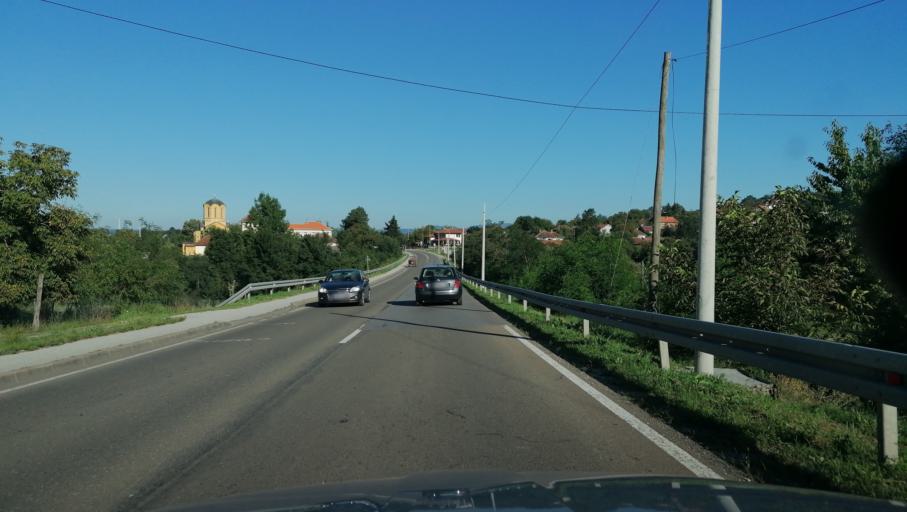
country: RS
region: Central Serbia
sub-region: Sumadijski Okrug
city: Knic
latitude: 43.9280
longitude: 20.7090
